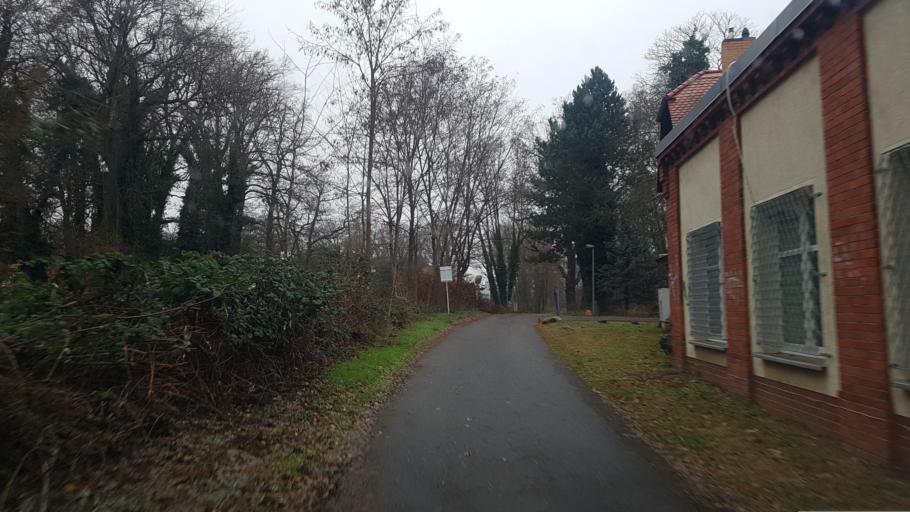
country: DE
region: Brandenburg
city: Cottbus
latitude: 51.7369
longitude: 14.3466
